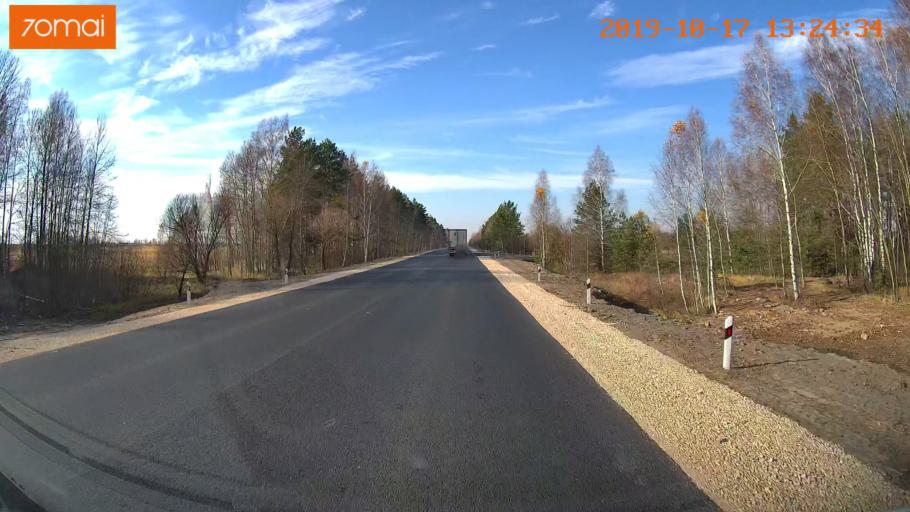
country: RU
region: Rjazan
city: Gus'-Zheleznyy
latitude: 55.0964
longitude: 40.9606
